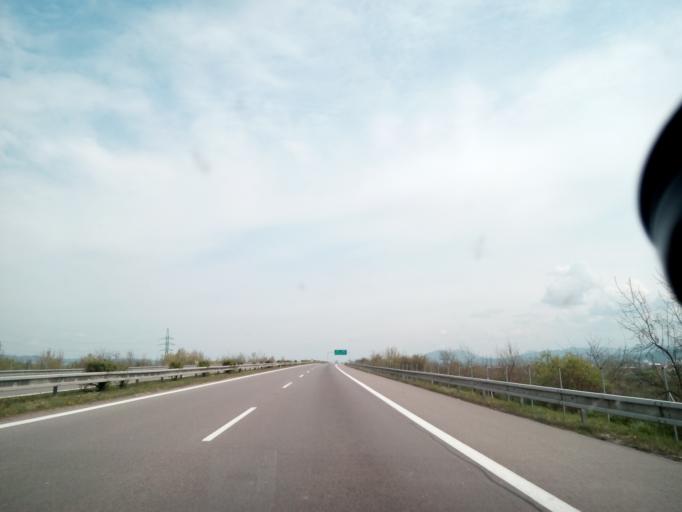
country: SK
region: Nitriansky
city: Nemsova
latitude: 48.9550
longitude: 18.1210
